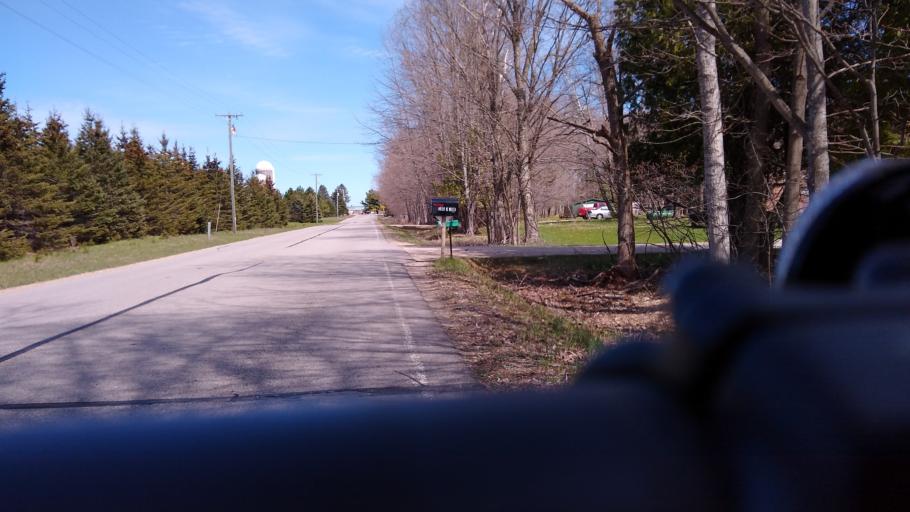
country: US
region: Michigan
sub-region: Delta County
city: Escanaba
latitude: 45.6955
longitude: -87.1569
